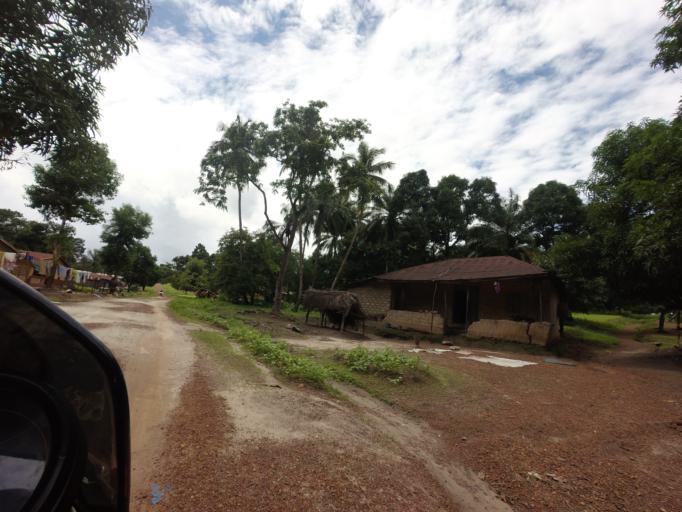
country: SL
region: Northern Province
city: Mambolo
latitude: 8.9763
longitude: -12.9968
